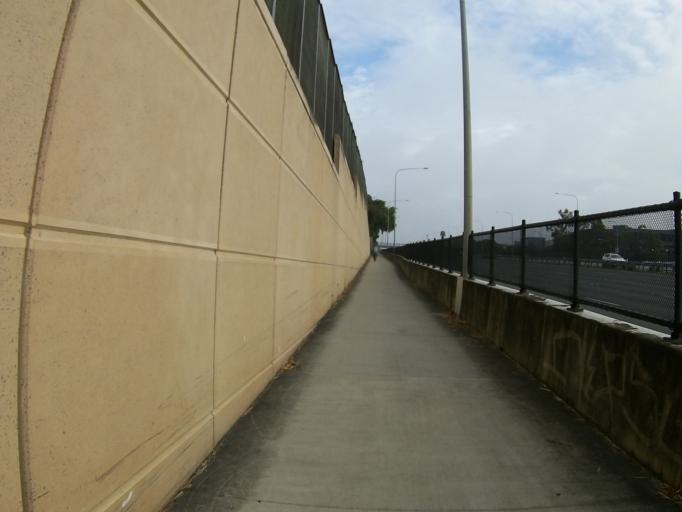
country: AU
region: Queensland
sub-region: Brisbane
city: Upper Mount Gravatt
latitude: -27.5673
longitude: 153.0853
